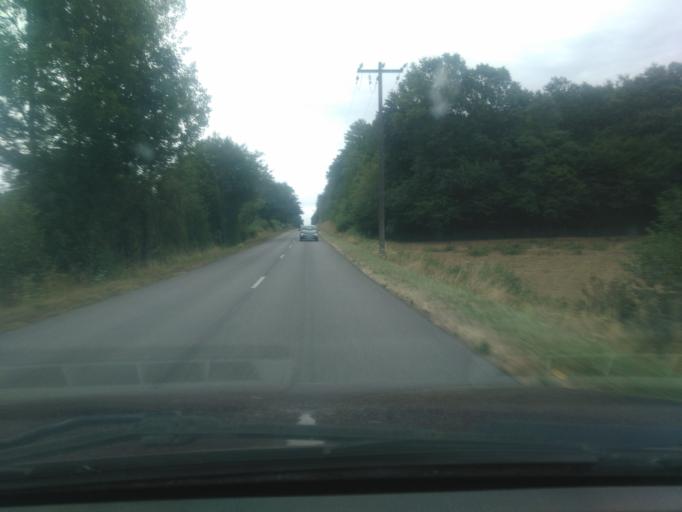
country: FR
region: Bourgogne
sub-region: Departement de la Nievre
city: Dornes
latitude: 46.7714
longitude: 3.3239
